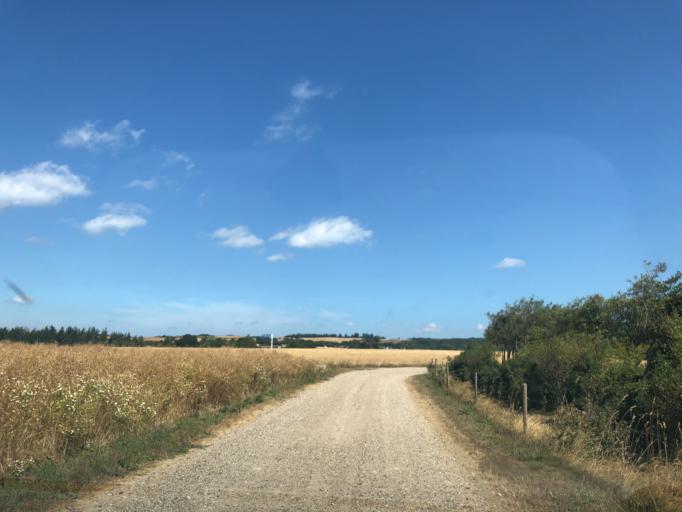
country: DK
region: North Denmark
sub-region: Morso Kommune
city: Nykobing Mors
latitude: 56.8121
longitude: 8.9931
